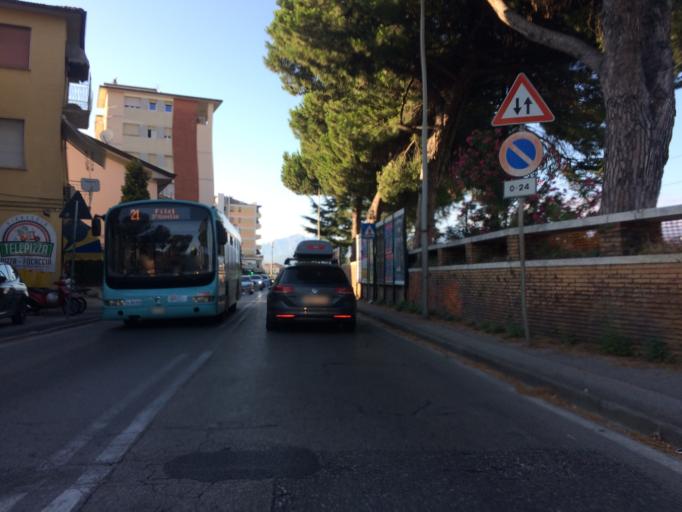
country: IT
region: Tuscany
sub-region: Provincia di Lucca
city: Viareggio
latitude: 43.8753
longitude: 10.2518
